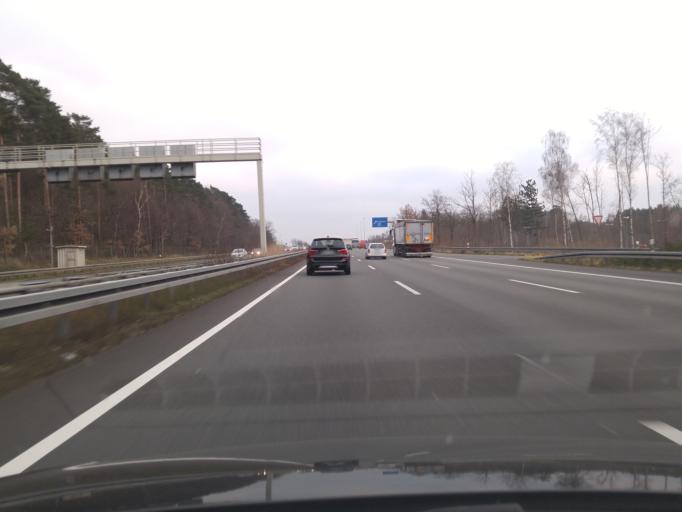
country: DE
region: Saxony-Anhalt
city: Harbke
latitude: 52.2235
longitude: 11.0469
